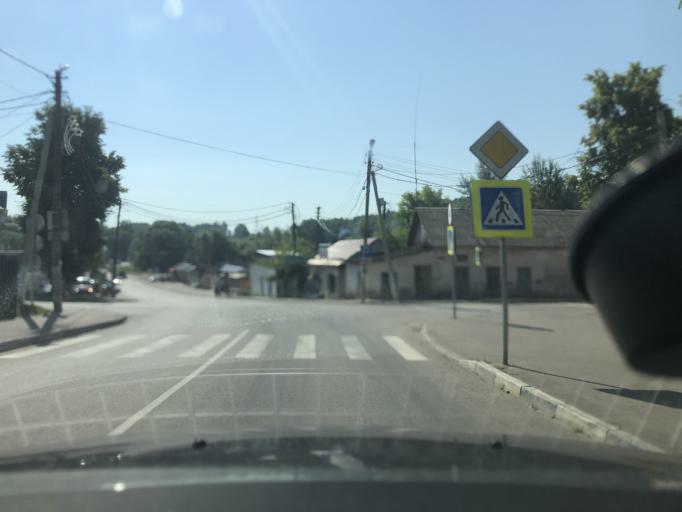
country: RU
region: Tula
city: Dubna
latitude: 54.1514
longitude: 36.9629
